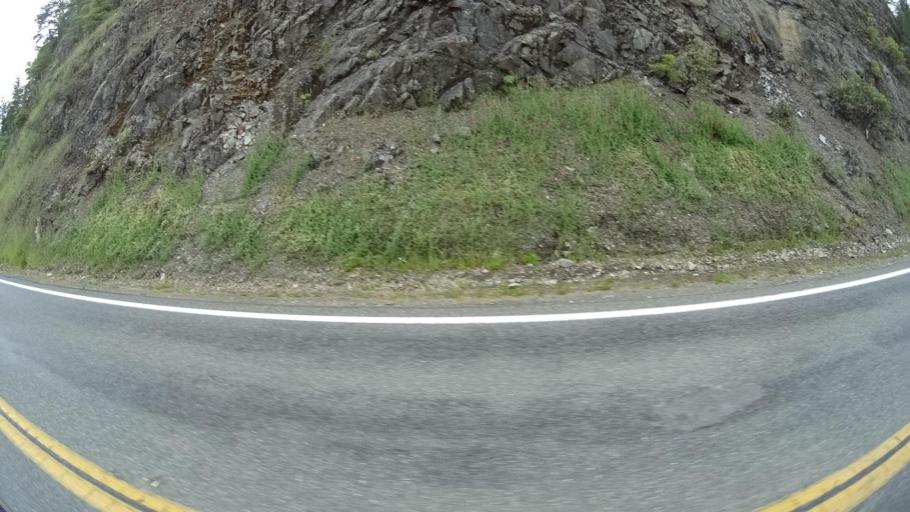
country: US
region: California
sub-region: Humboldt County
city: Willow Creek
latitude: 40.9990
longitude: -123.6258
